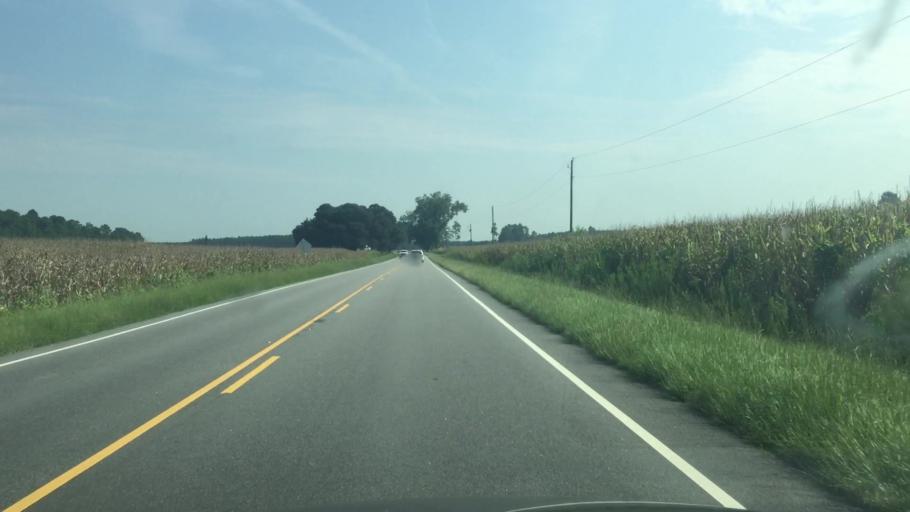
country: US
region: North Carolina
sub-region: Columbus County
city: Tabor City
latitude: 34.1666
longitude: -78.8442
